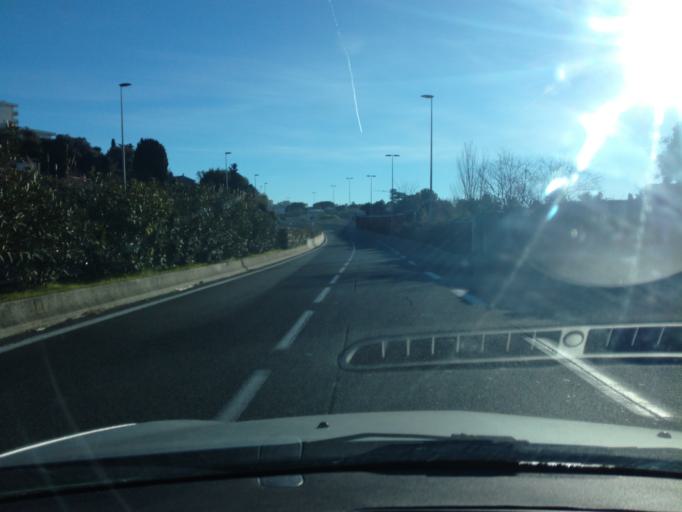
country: FR
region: Provence-Alpes-Cote d'Azur
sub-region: Departement des Alpes-Maritimes
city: Antibes
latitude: 43.5783
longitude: 7.1004
